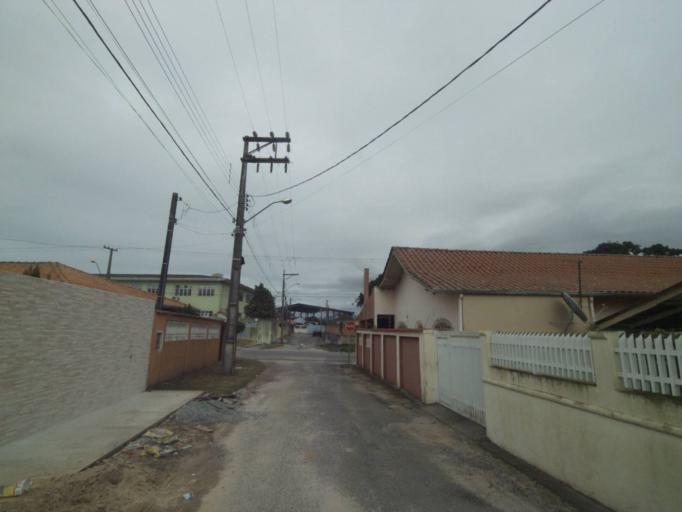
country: BR
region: Parana
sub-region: Paranagua
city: Paranagua
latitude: -25.5184
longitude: -48.5313
